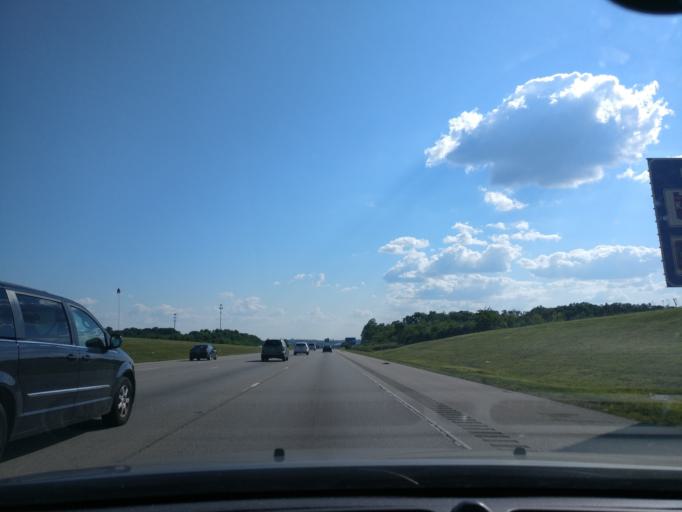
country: US
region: Ohio
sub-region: Warren County
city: Springboro
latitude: 39.5742
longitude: -84.2571
